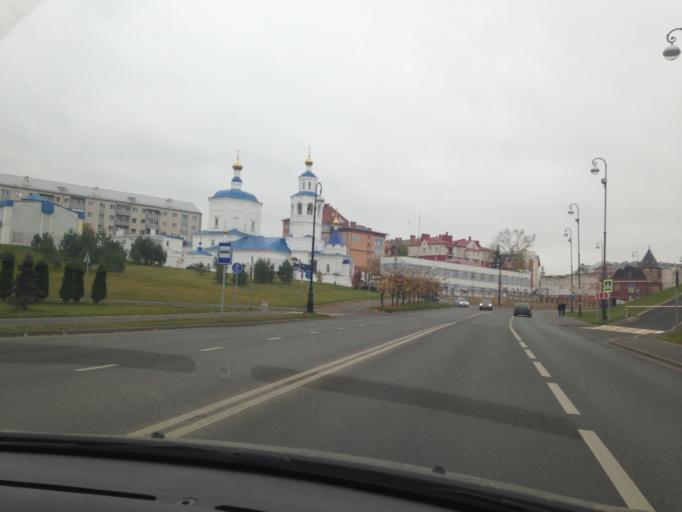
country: RU
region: Tatarstan
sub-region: Gorod Kazan'
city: Kazan
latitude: 55.8001
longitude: 49.1085
